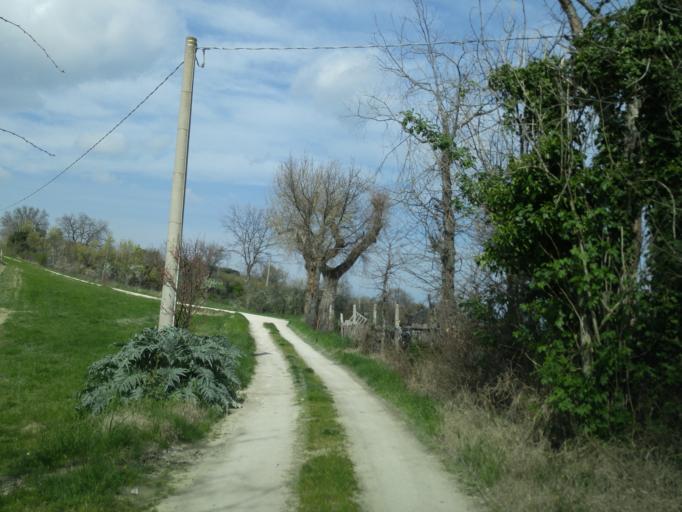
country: IT
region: The Marches
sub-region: Provincia di Pesaro e Urbino
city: Villanova
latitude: 43.7212
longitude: 12.9324
